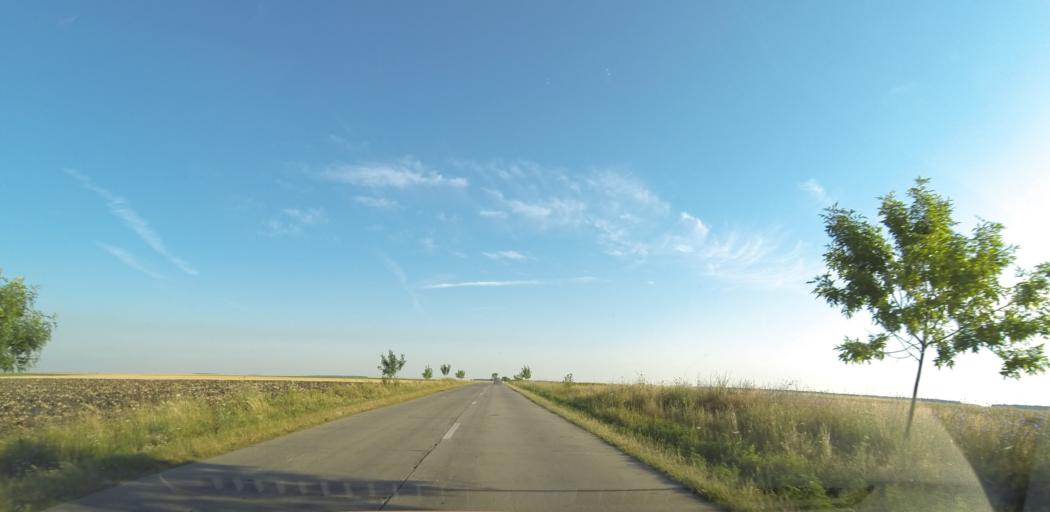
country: RO
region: Dolj
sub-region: Comuna Murgasu
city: Murgasi
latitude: 44.4550
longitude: 23.8483
